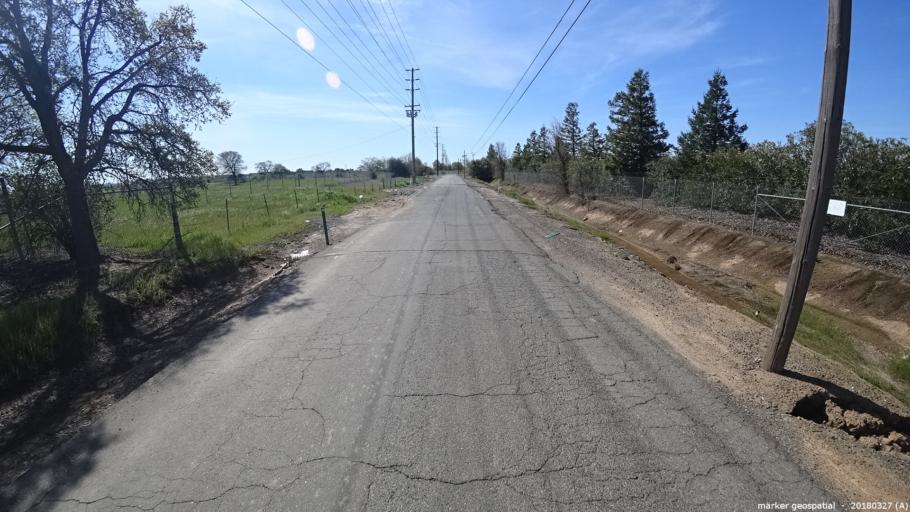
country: US
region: California
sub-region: Sacramento County
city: Rosemont
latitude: 38.5227
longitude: -121.3442
